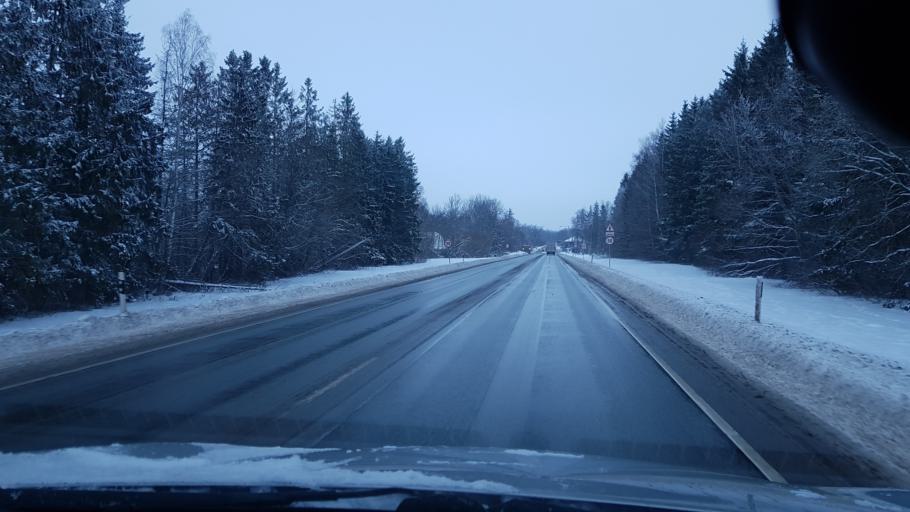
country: EE
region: Harju
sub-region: Harku vald
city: Tabasalu
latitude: 59.3766
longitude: 24.5357
